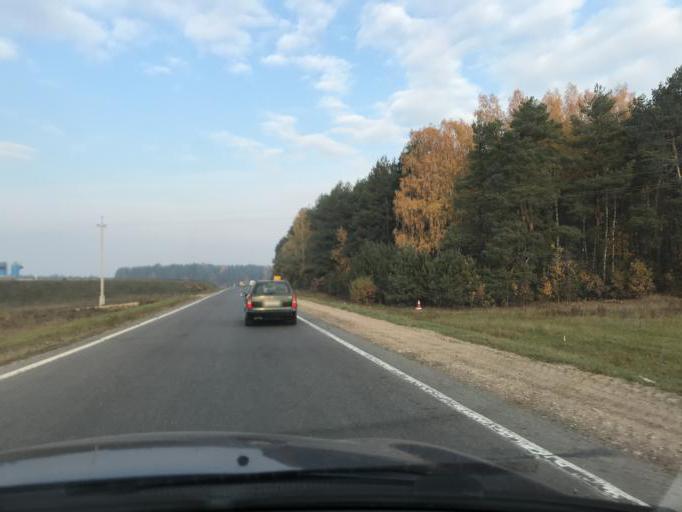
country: BY
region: Grodnenskaya
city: Lida
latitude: 53.8302
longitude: 25.3569
